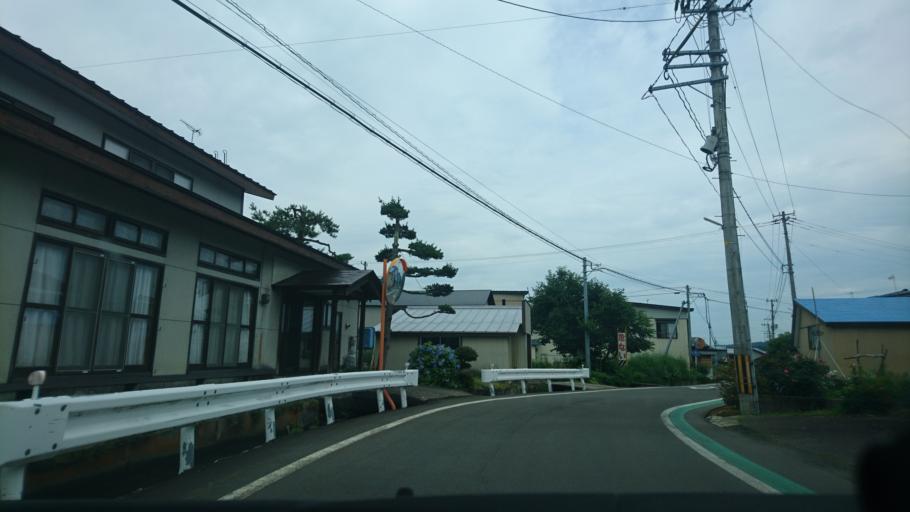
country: JP
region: Akita
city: Yuzawa
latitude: 39.1797
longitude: 140.6470
